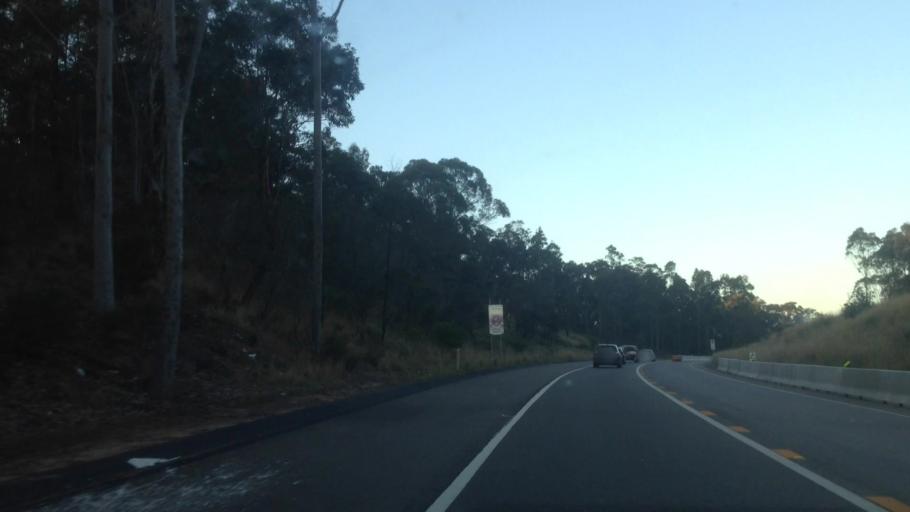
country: AU
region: New South Wales
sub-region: Wyong Shire
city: Jilliby
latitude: -33.2175
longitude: 151.4410
